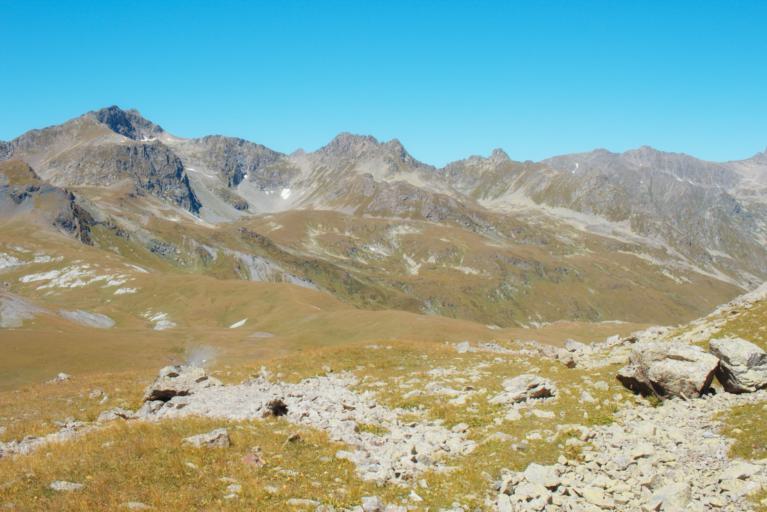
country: RU
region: Karachayevo-Cherkesiya
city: Nizhniy Arkhyz
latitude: 43.6028
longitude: 41.1678
